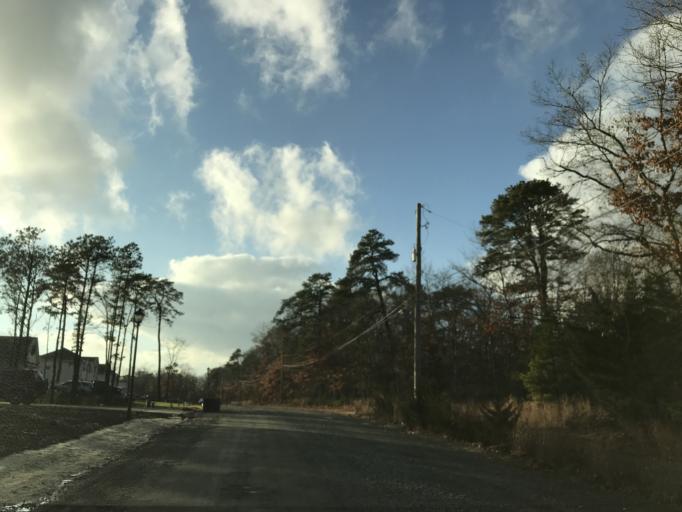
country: US
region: New Jersey
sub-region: Ocean County
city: Waretown
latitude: 39.7919
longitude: -74.2282
